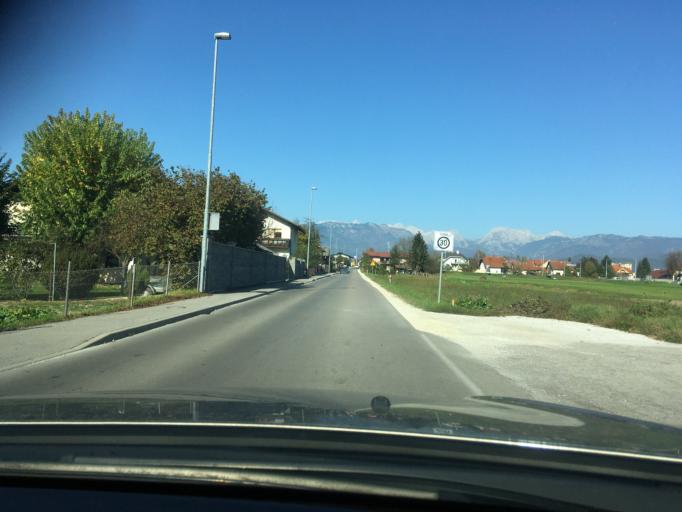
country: SI
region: Domzale
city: Vir
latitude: 46.1454
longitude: 14.6083
